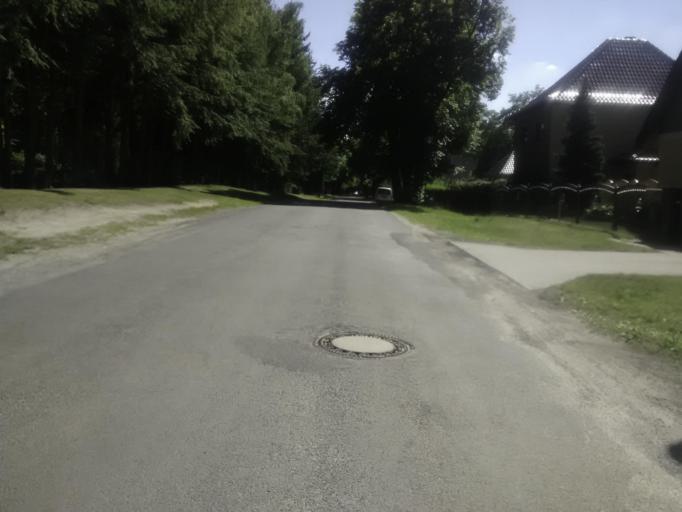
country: DE
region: Brandenburg
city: Hohen Neuendorf
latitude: 52.6763
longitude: 13.2741
